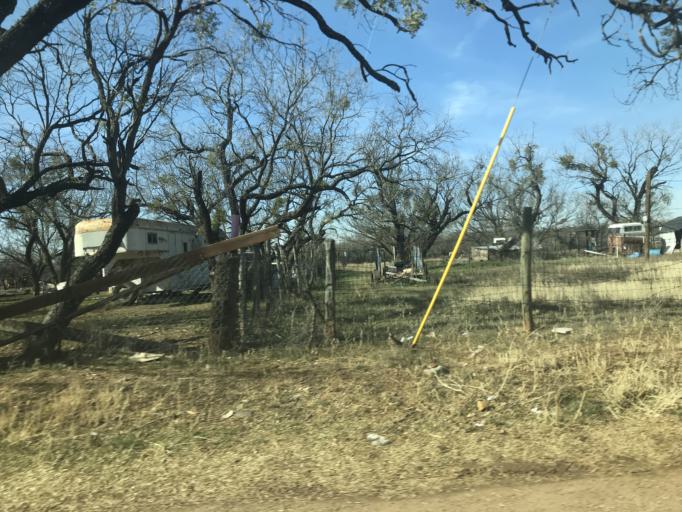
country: US
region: Texas
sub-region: Taylor County
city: Abilene
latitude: 32.4962
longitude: -99.7426
